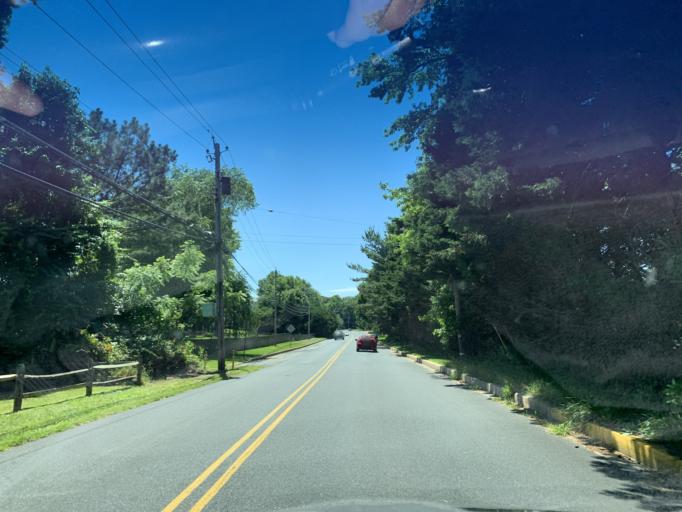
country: US
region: Maryland
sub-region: Harford County
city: Havre de Grace
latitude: 39.5537
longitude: -76.1144
